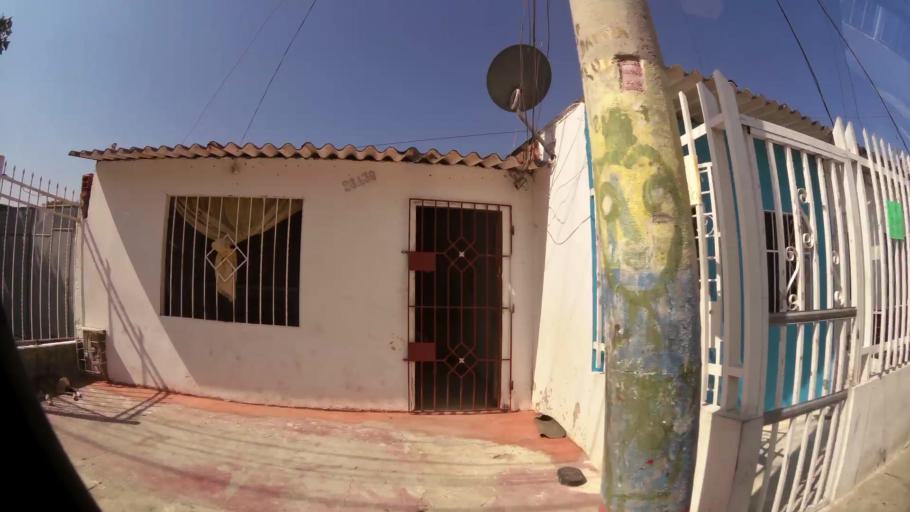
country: CO
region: Atlantico
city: Barranquilla
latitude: 10.9739
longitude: -74.8352
